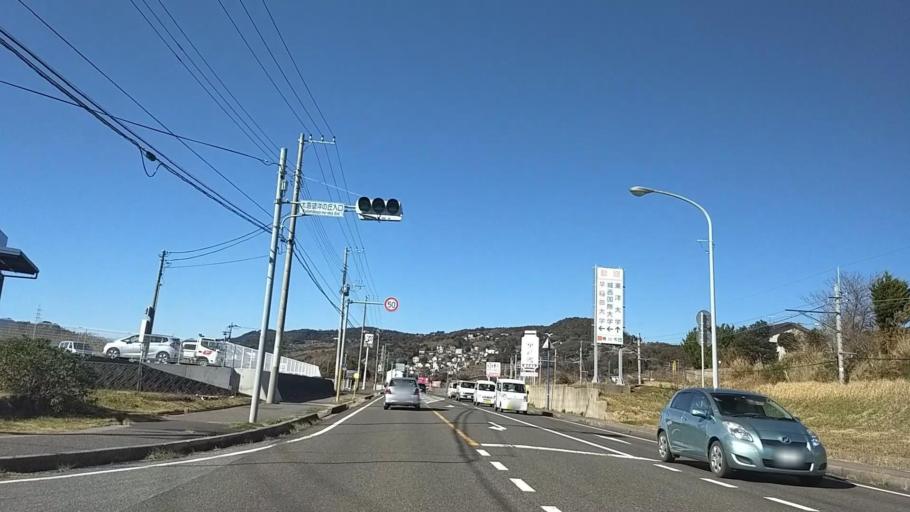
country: JP
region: Chiba
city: Kawaguchi
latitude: 35.0862
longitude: 140.0935
